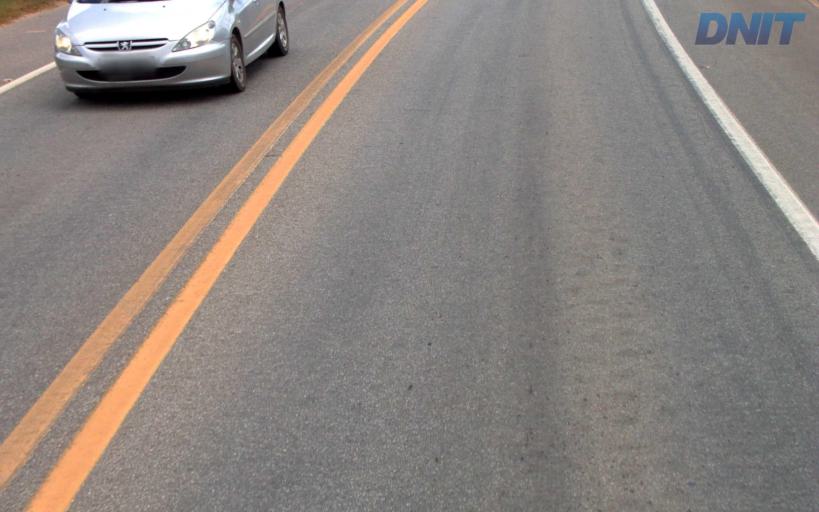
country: BR
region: Minas Gerais
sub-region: Governador Valadares
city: Governador Valadares
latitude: -18.8487
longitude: -41.9838
